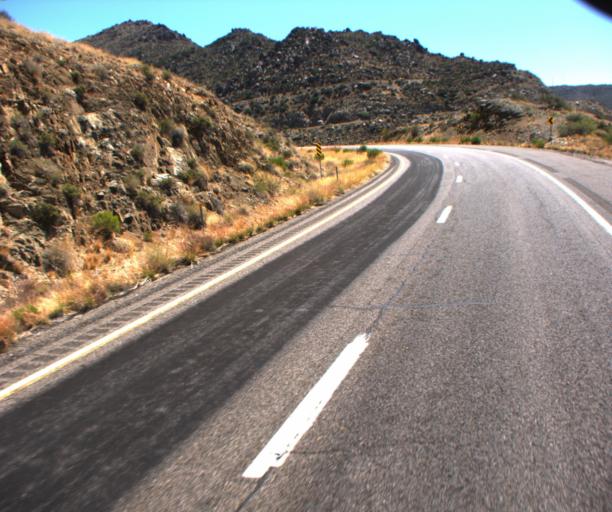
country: US
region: Arizona
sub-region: Yavapai County
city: Congress
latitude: 34.2035
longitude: -112.7889
